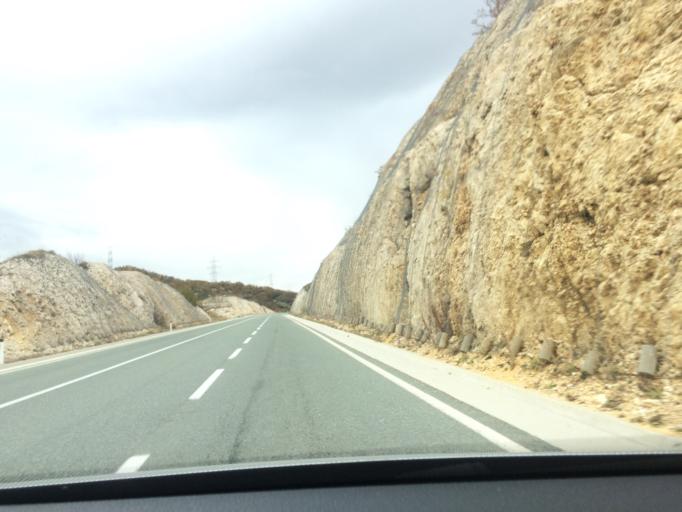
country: ME
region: Opstina Savnik
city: Savnik
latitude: 42.9906
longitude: 19.0739
